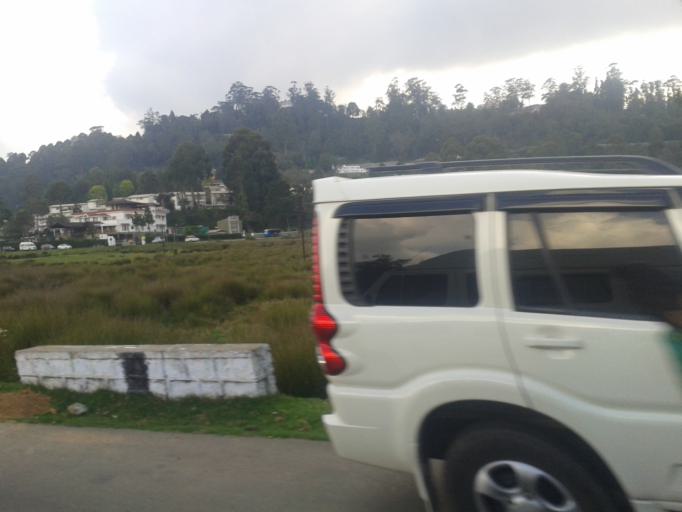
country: IN
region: Tamil Nadu
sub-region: Dindigul
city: Kodaikanal
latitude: 10.2319
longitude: 77.4822
